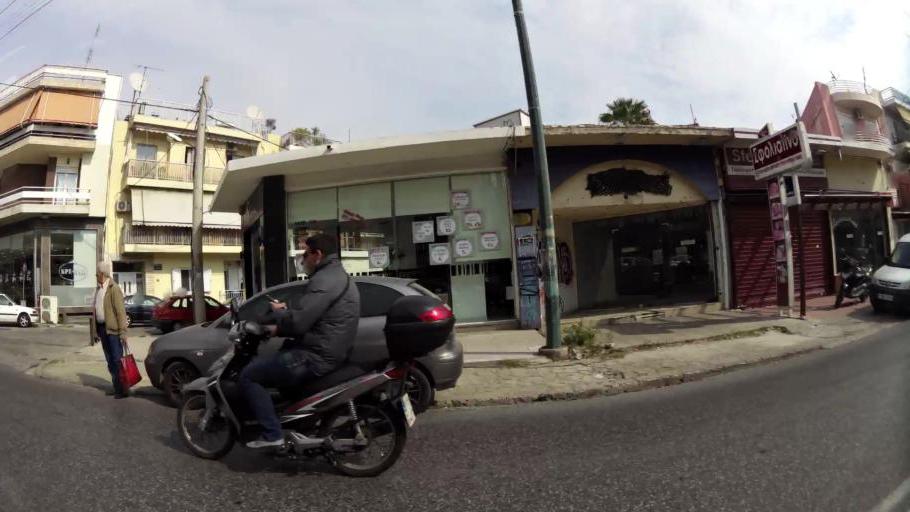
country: GR
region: Attica
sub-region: Nomarchia Athinas
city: Peristeri
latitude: 38.0251
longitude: 23.6829
